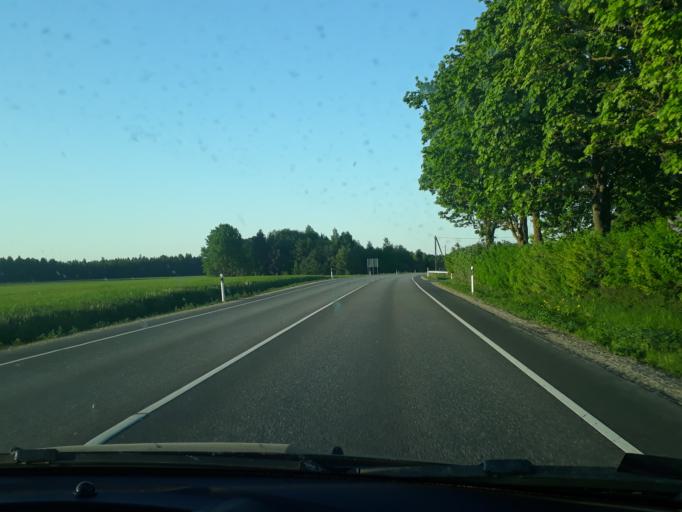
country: EE
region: Paernumaa
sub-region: Tootsi vald
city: Tootsi
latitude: 58.5549
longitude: 24.8567
